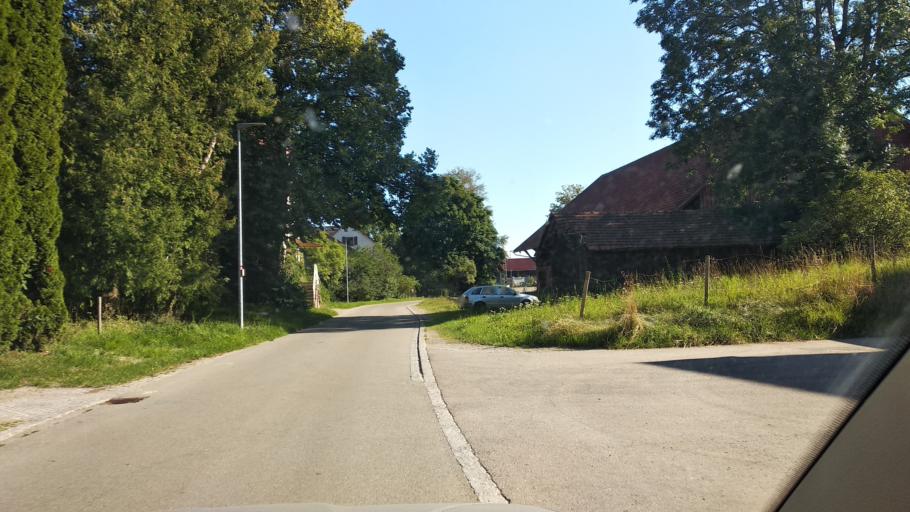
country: DE
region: Baden-Wuerttemberg
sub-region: Tuebingen Region
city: Leutkirch im Allgau
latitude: 47.8014
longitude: 10.0489
